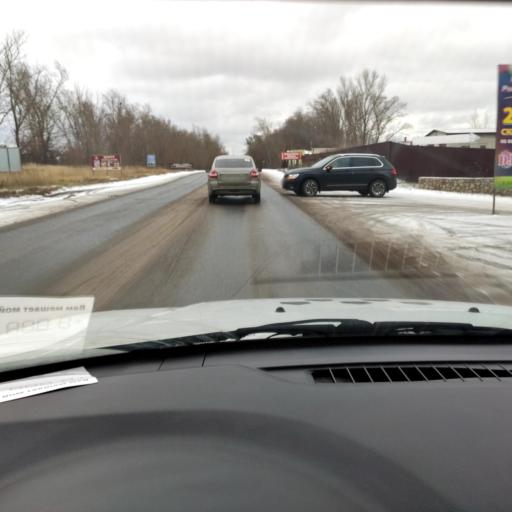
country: RU
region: Samara
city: Tol'yatti
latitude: 53.5549
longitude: 49.3939
